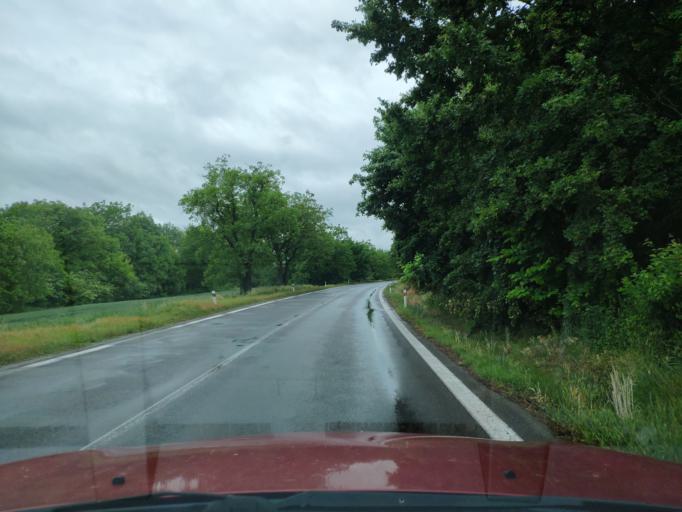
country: HU
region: Borsod-Abauj-Zemplen
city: Karcsa
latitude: 48.3907
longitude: 21.7737
